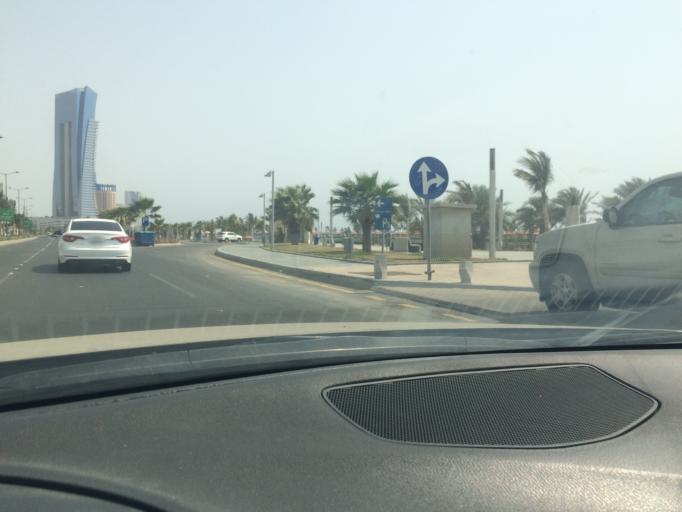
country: SA
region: Makkah
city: Jeddah
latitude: 21.5856
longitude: 39.1087
